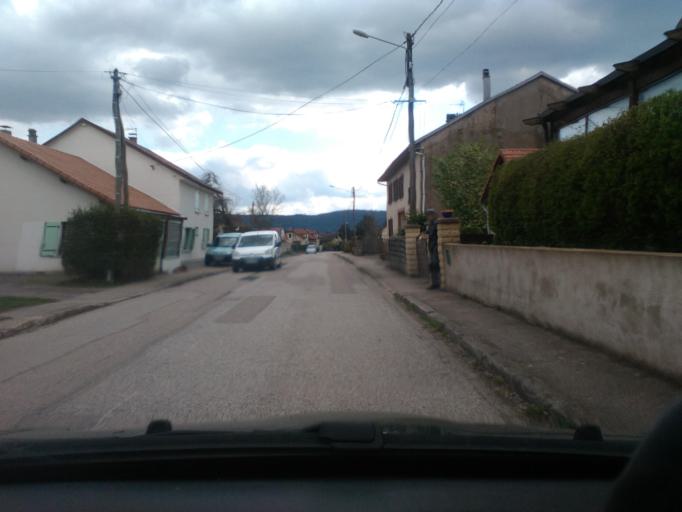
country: FR
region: Lorraine
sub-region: Departement des Vosges
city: Etival-Clairefontaine
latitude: 48.3437
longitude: 6.8273
